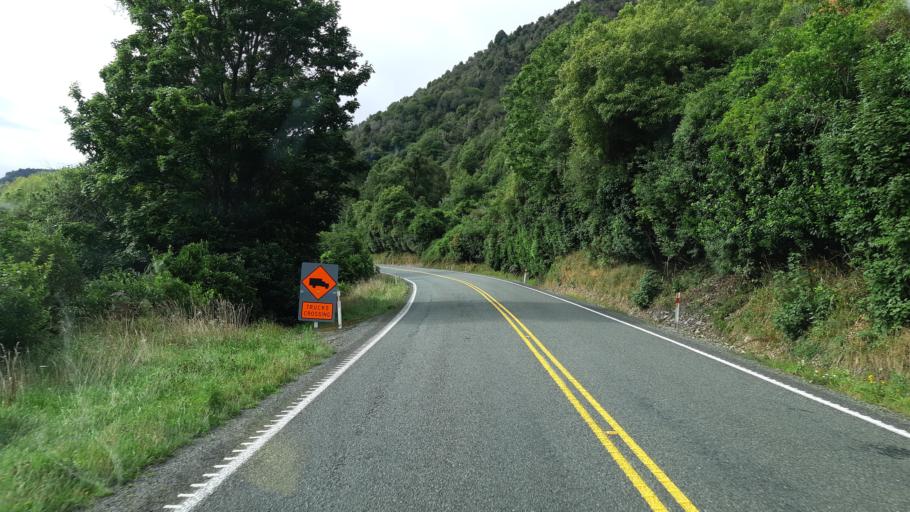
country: NZ
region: West Coast
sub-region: Buller District
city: Westport
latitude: -41.7748
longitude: 172.2399
